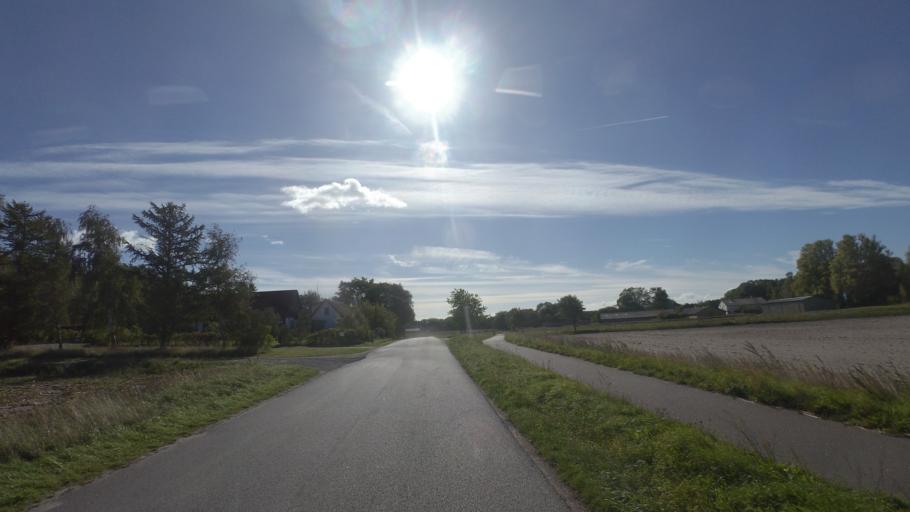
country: DK
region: Capital Region
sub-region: Bornholm Kommune
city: Akirkeby
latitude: 55.0105
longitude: 14.9917
